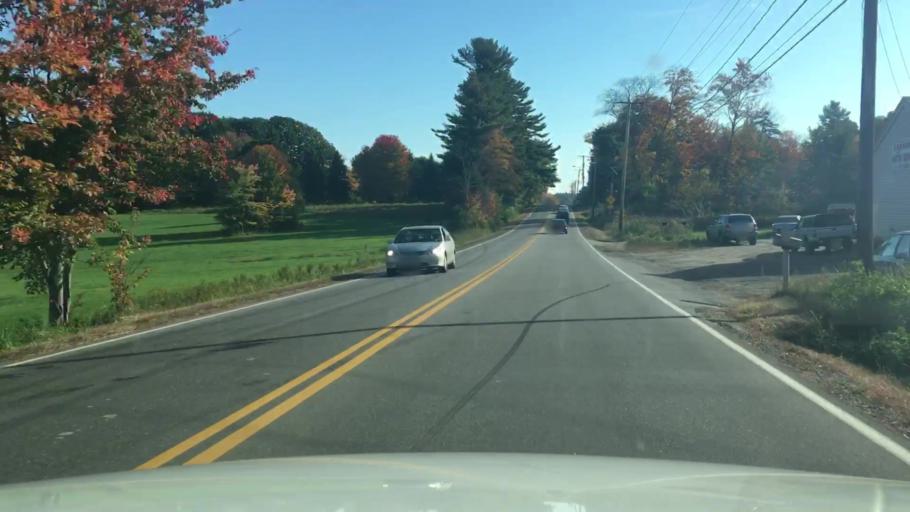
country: US
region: Maine
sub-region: Cumberland County
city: Westbrook
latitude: 43.6480
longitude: -70.3746
